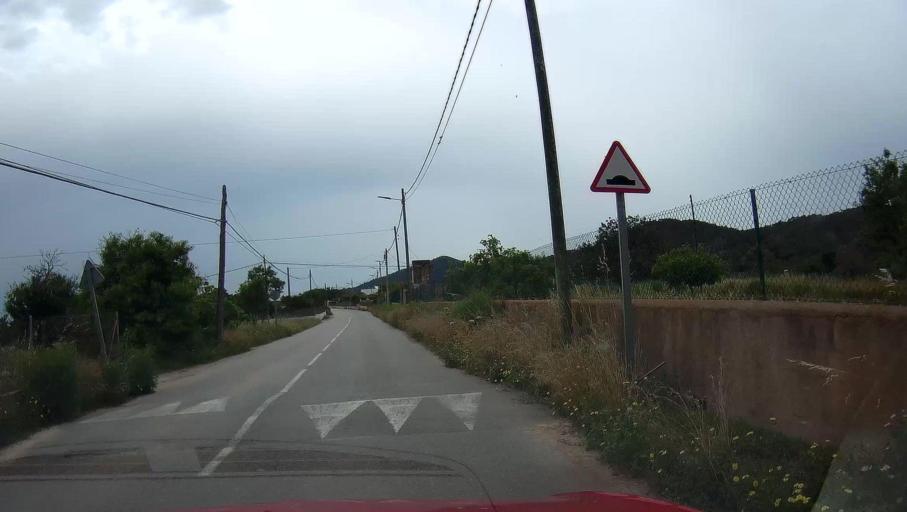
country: ES
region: Balearic Islands
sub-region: Illes Balears
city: Sant Josep de sa Talaia
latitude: 38.8738
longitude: 1.3504
